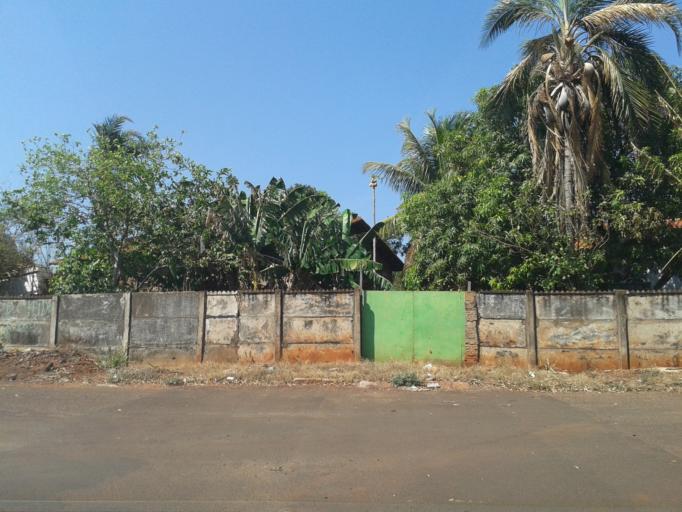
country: BR
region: Minas Gerais
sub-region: Ituiutaba
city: Ituiutaba
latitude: -18.9609
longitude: -49.4510
